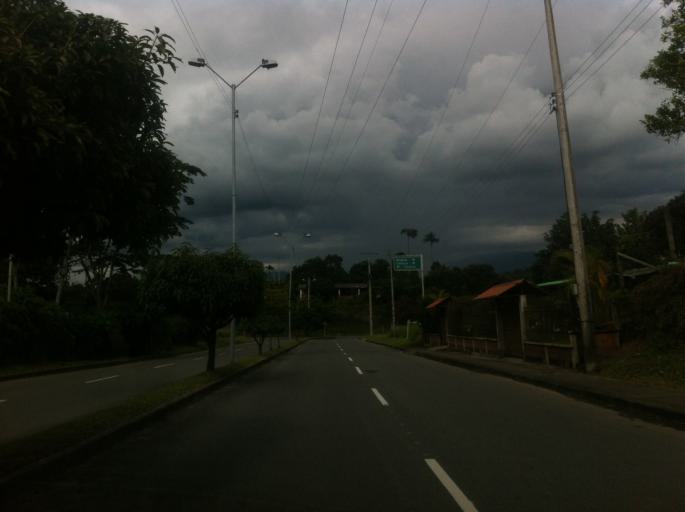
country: CO
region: Quindio
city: Circasia
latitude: 4.5814
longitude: -75.6366
